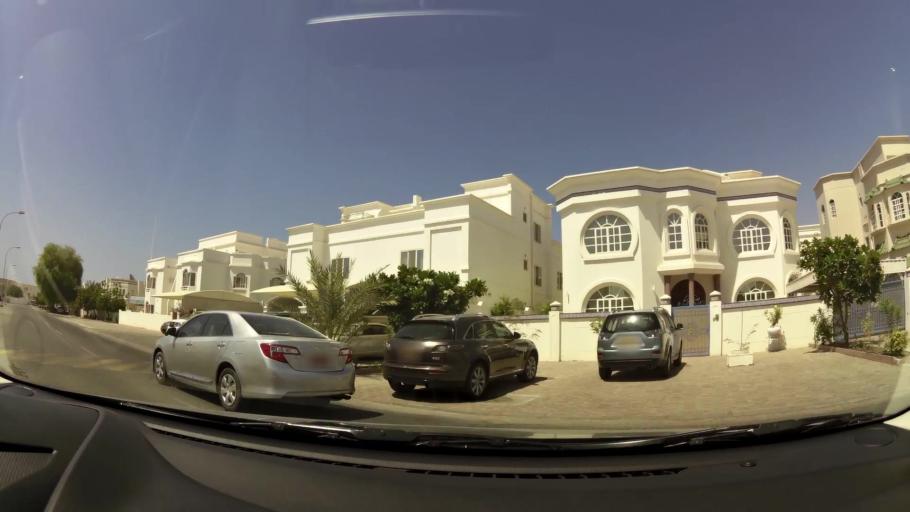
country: OM
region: Muhafazat Masqat
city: Bawshar
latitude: 23.5980
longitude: 58.3652
